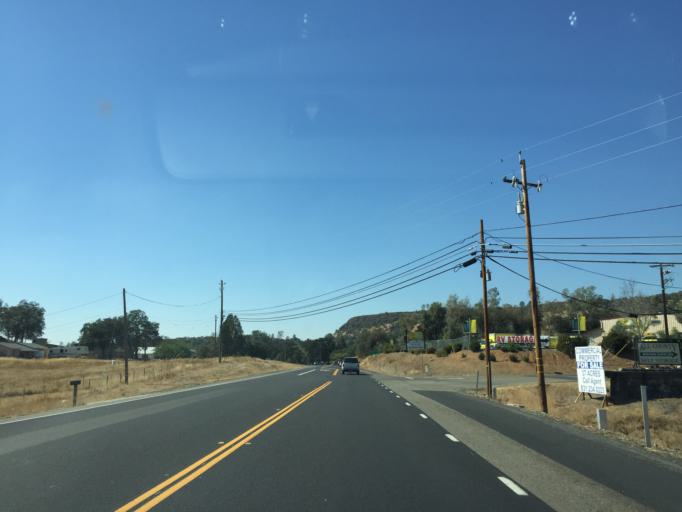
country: US
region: California
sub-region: Tuolumne County
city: Jamestown
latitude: 37.9369
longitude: -120.4402
